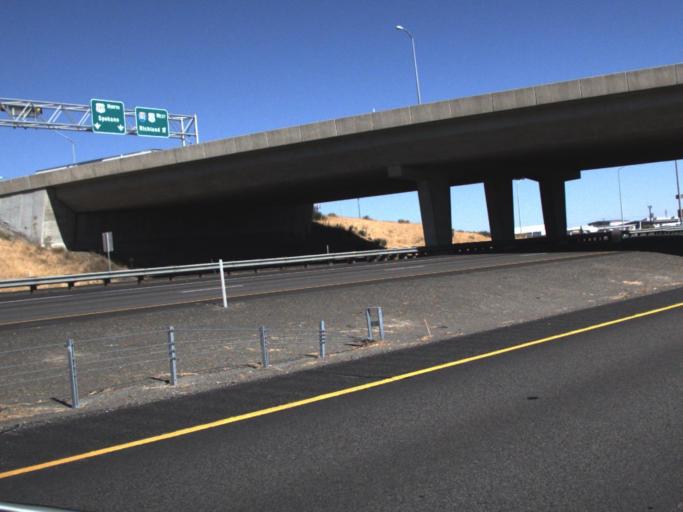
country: US
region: Washington
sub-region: Franklin County
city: Pasco
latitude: 46.2517
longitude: -119.0831
